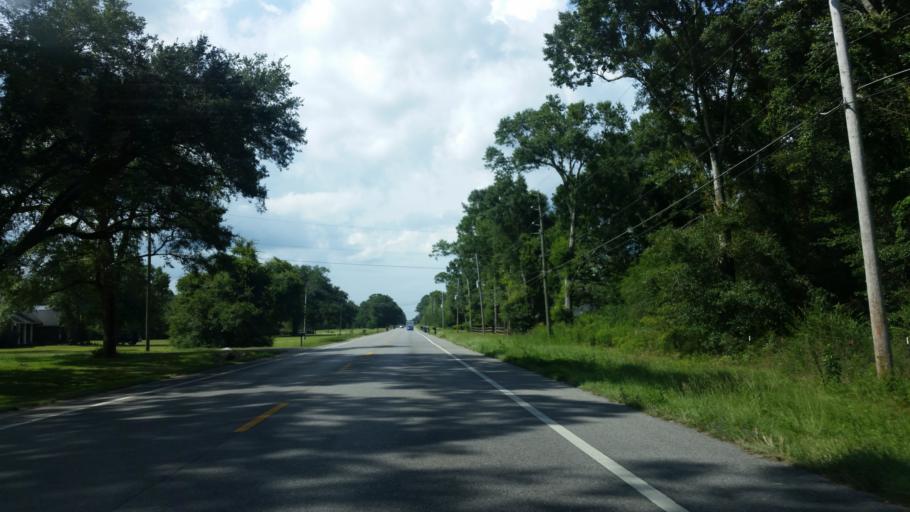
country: US
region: Florida
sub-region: Escambia County
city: Cantonment
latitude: 30.5816
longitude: -87.3494
